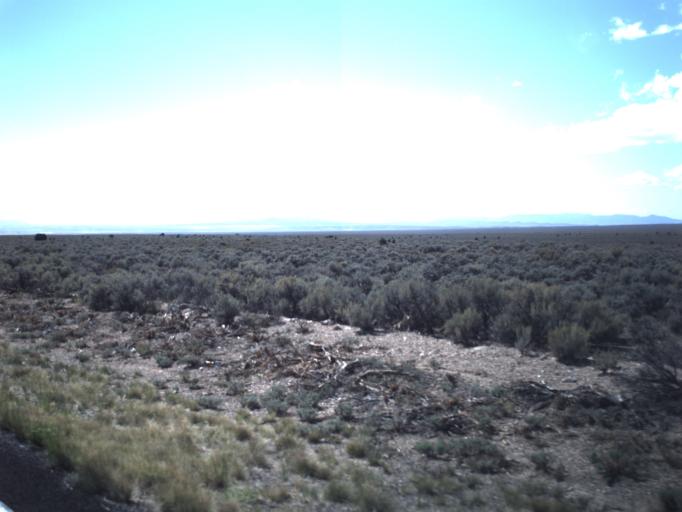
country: US
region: Utah
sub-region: Iron County
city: Enoch
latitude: 38.0061
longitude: -112.9978
